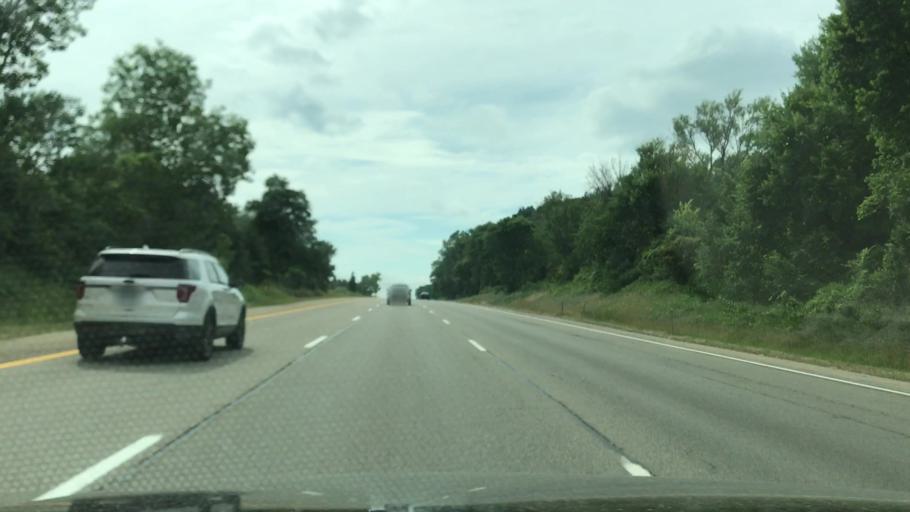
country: US
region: Michigan
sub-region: Kent County
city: Comstock Park
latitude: 43.0186
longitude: -85.6969
